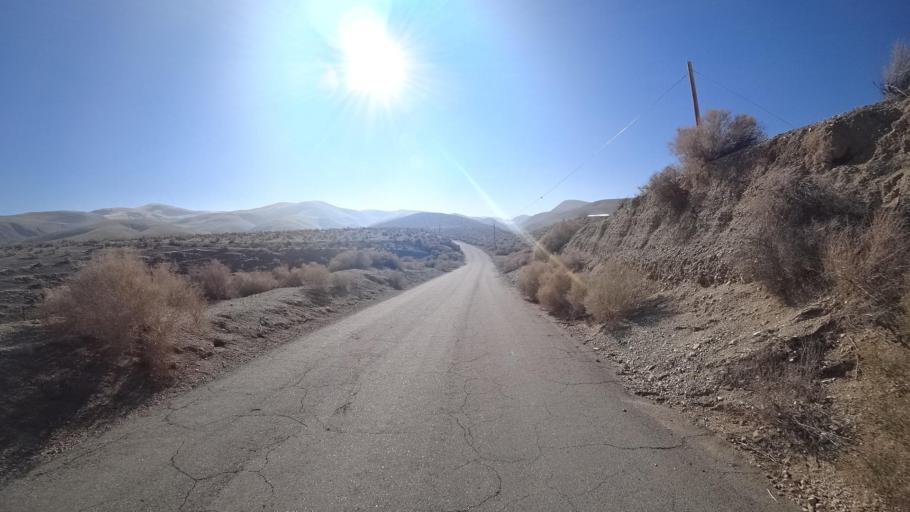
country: US
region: California
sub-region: Kern County
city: Maricopa
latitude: 34.9904
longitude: -119.3914
